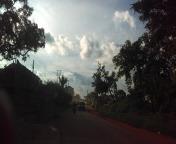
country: UG
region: Central Region
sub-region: Wakiso District
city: Kajansi
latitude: 0.2565
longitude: 32.5607
